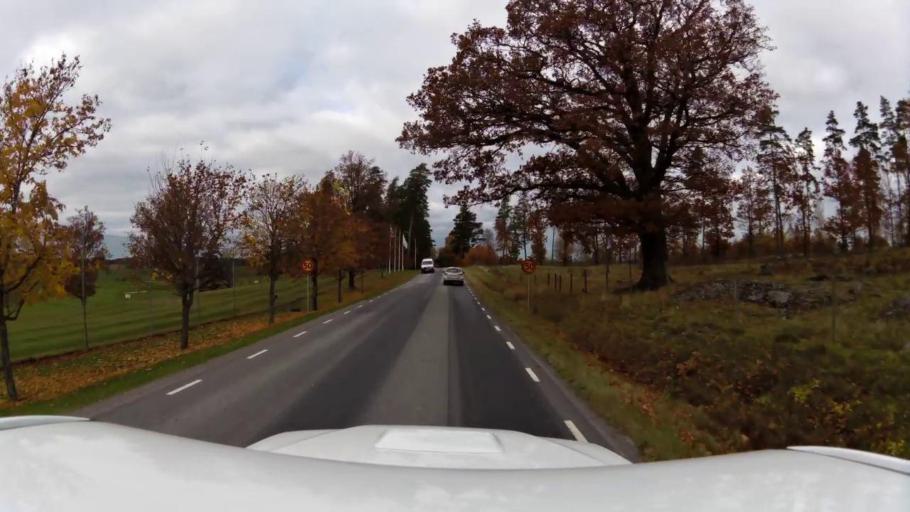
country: SE
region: OEstergoetland
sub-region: Linkopings Kommun
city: Linghem
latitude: 58.4133
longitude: 15.7481
